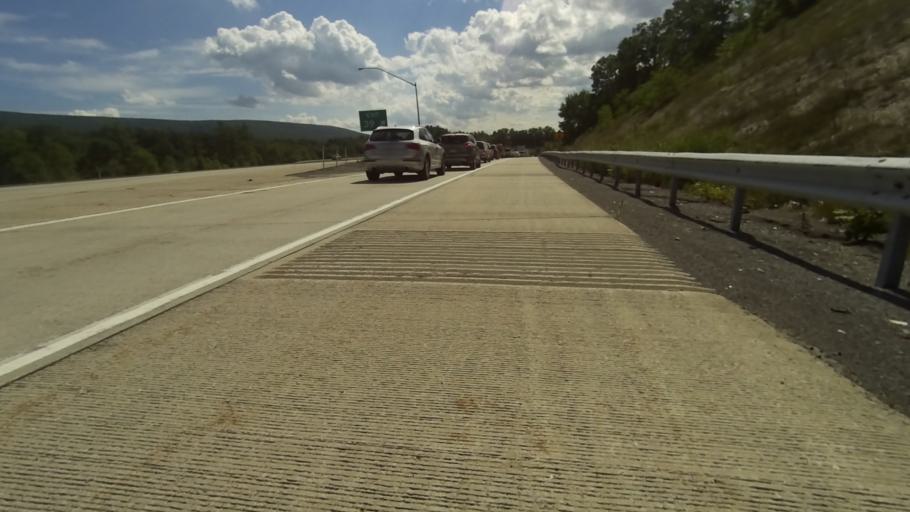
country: US
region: Pennsylvania
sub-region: Blair County
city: Bellwood
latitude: 40.5648
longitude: -78.3268
